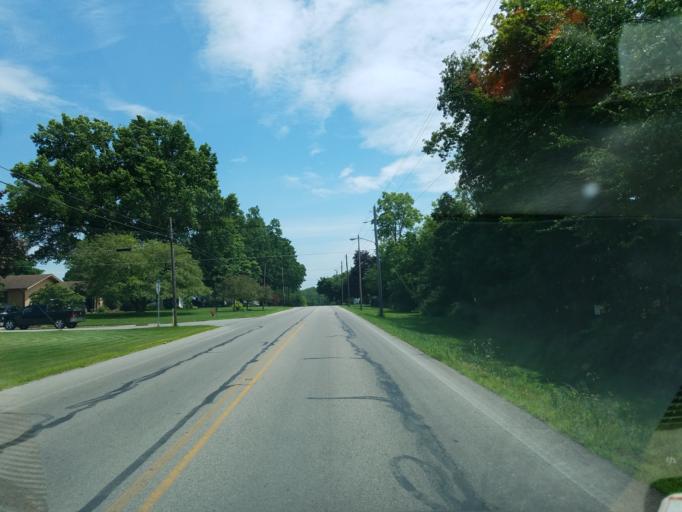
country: US
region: Ohio
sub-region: Ashland County
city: Ashland
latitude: 40.8788
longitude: -82.3386
